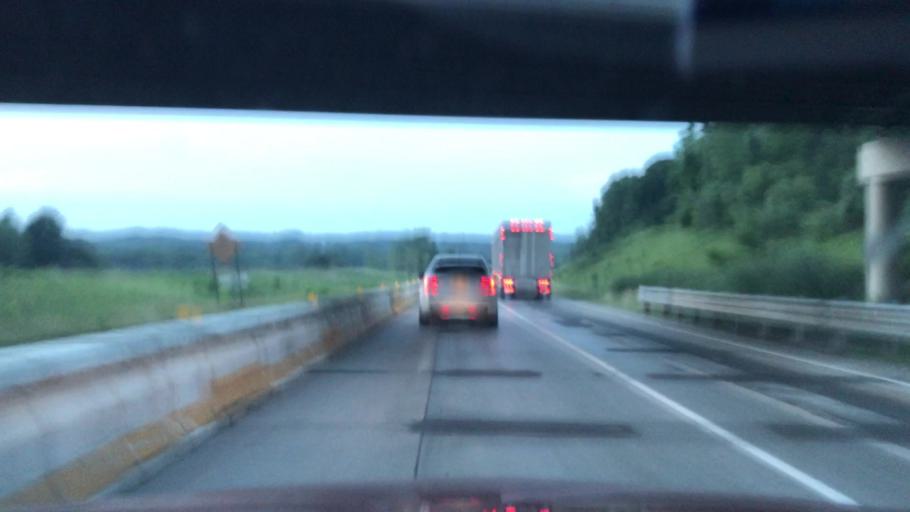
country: US
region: Michigan
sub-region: Kent County
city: Rockford
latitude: 43.1462
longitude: -85.5877
